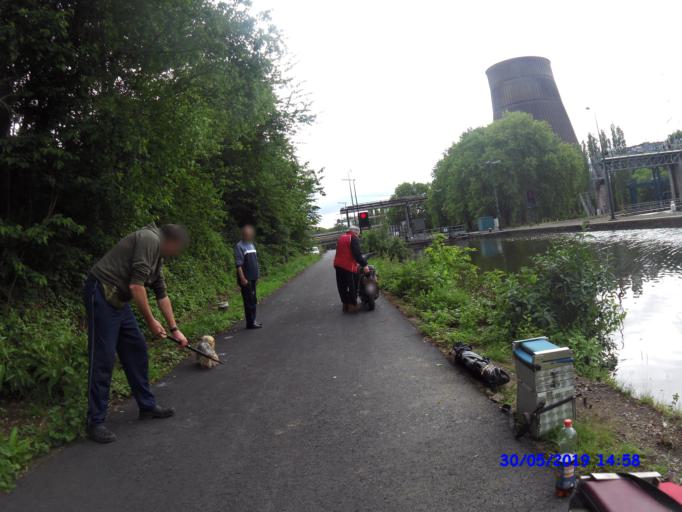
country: BE
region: Wallonia
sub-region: Province du Hainaut
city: Charleroi
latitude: 50.3927
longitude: 4.3795
